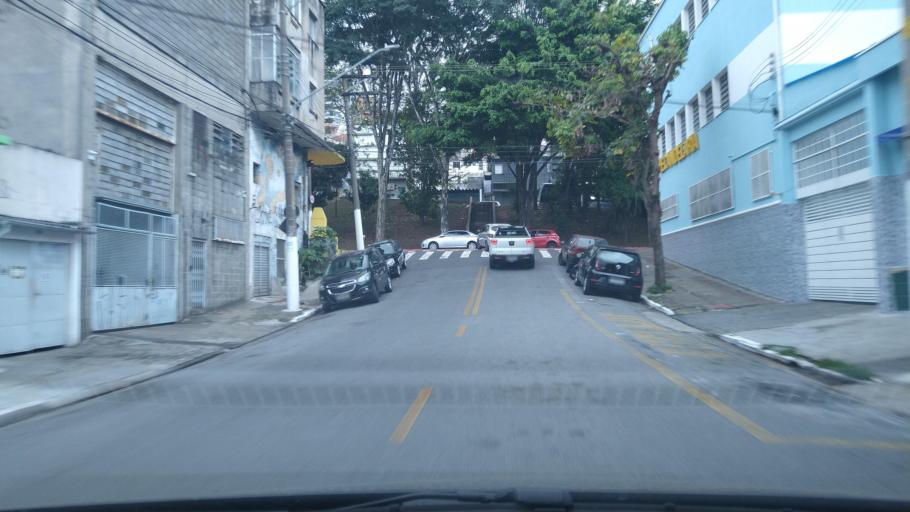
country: BR
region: Sao Paulo
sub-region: Sao Paulo
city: Sao Paulo
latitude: -23.5124
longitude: -46.5864
